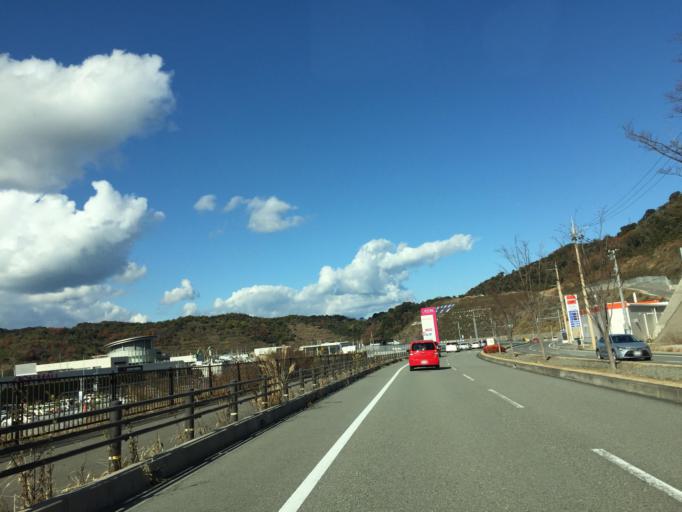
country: JP
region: Wakayama
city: Wakayama-shi
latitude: 34.2742
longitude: 135.1507
